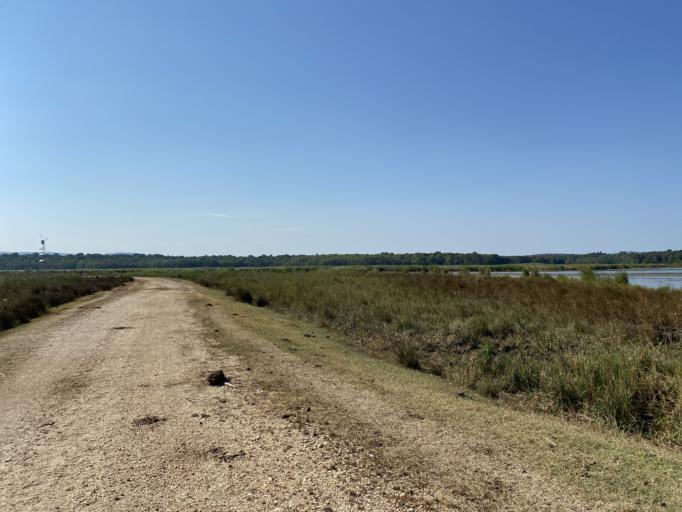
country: TR
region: Kirklareli
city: Igneada
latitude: 41.8615
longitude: 27.9720
